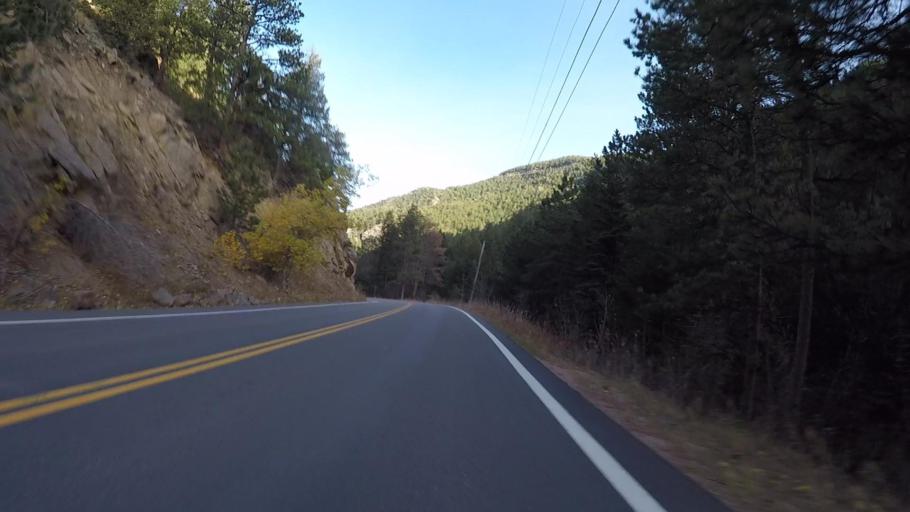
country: US
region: Colorado
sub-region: Boulder County
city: Boulder
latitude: 40.0750
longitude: -105.4041
